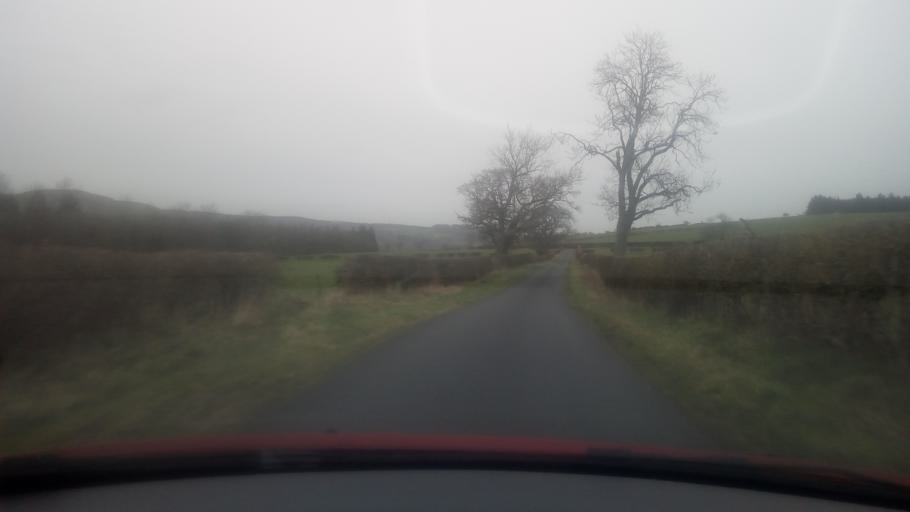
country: GB
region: Scotland
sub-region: The Scottish Borders
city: Hawick
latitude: 55.4435
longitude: -2.6882
